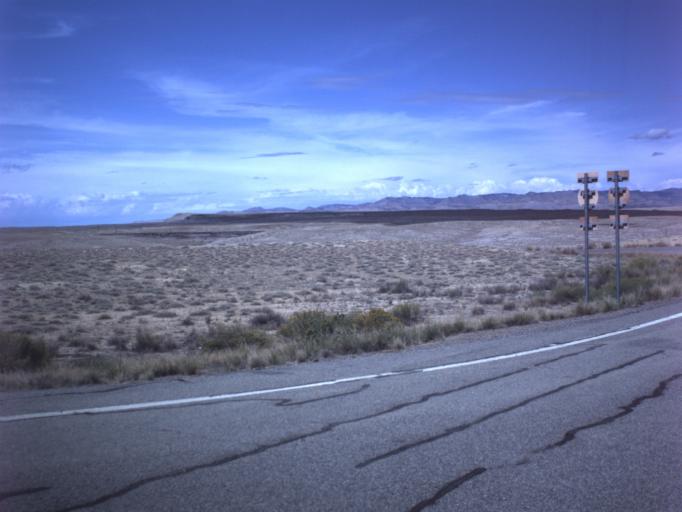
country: US
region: Utah
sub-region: Grand County
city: Moab
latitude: 38.9390
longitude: -109.4083
